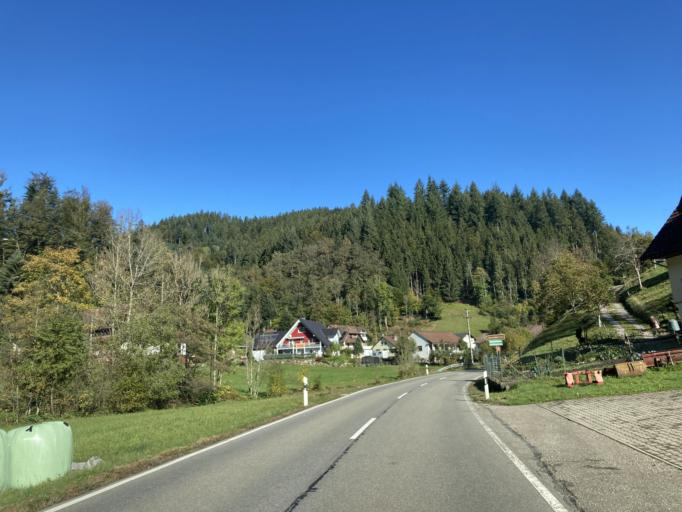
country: DE
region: Baden-Wuerttemberg
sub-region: Karlsruhe Region
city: Bad Rippoldsau-Schapbach
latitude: 48.4023
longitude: 8.3114
